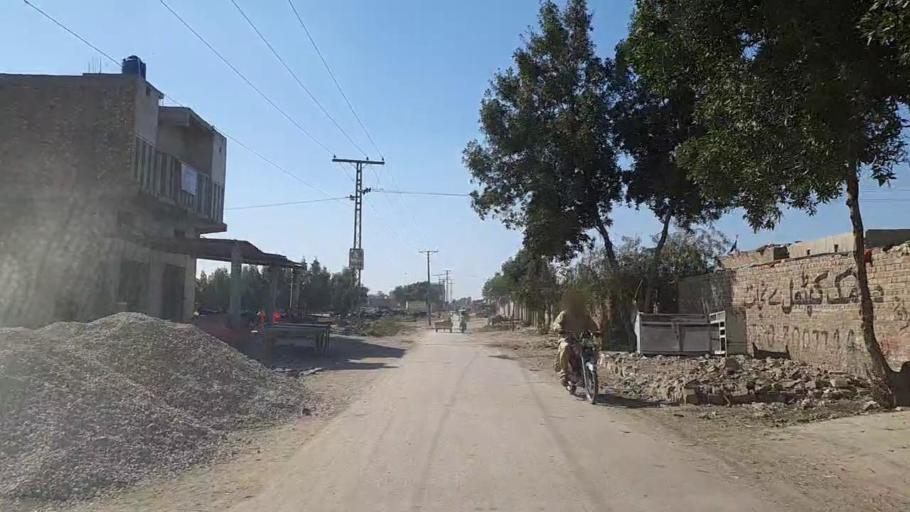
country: PK
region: Sindh
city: Nawabshah
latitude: 26.2440
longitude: 68.4244
